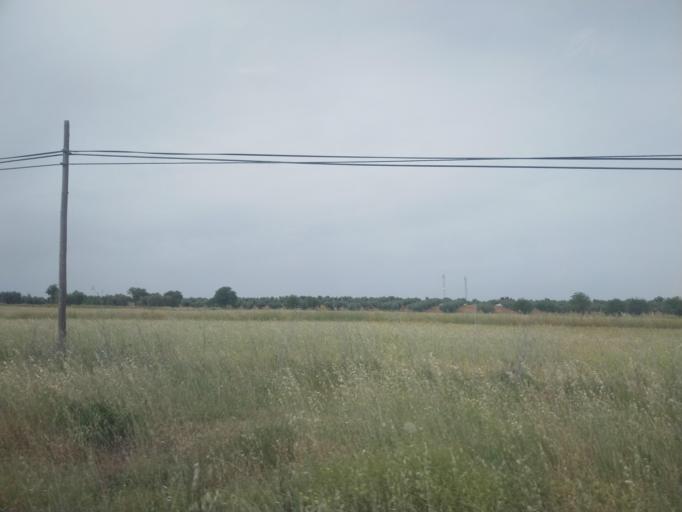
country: ES
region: Castille-La Mancha
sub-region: Province of Toledo
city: Casasbuenas
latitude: 39.7622
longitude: -4.1339
